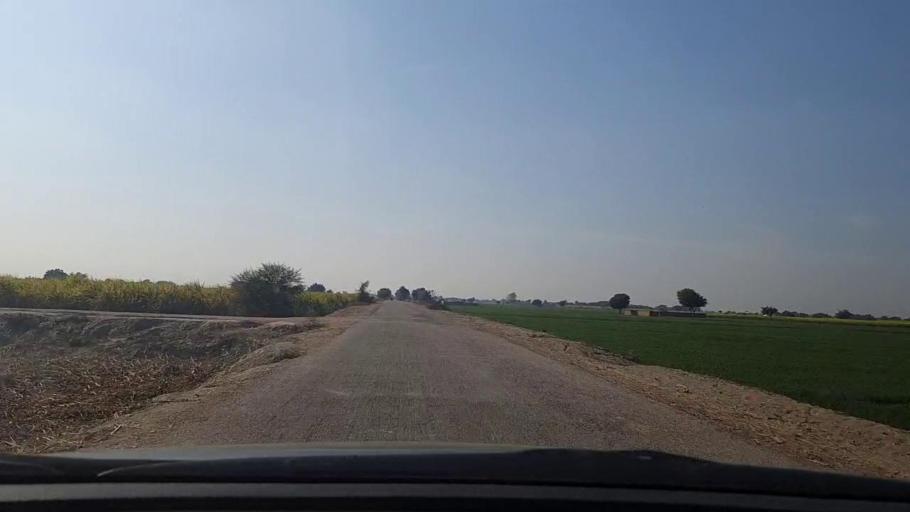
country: PK
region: Sindh
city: Daulatpur
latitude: 26.3203
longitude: 68.0361
